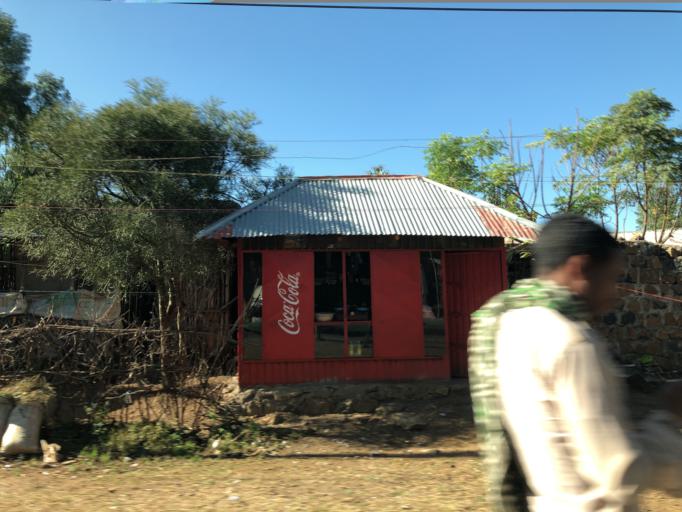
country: ET
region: Amhara
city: Gondar
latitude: 12.4756
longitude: 37.4816
